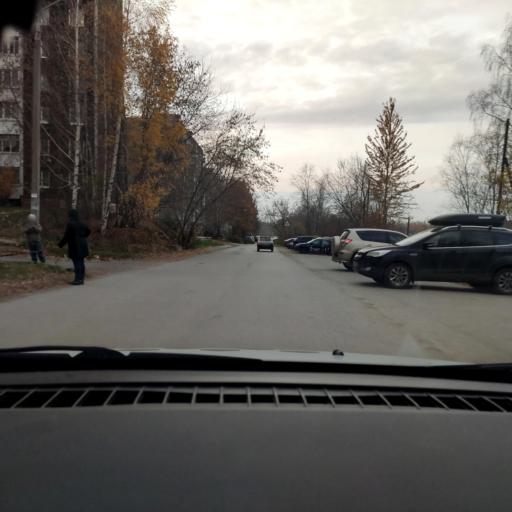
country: RU
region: Perm
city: Perm
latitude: 58.1100
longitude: 56.3828
